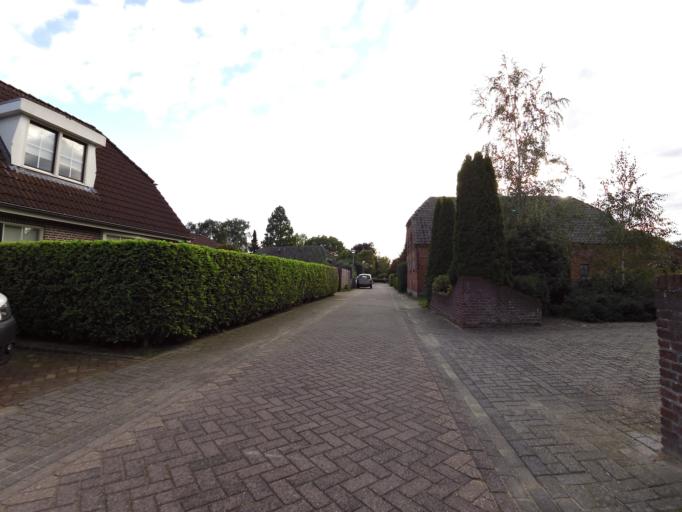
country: NL
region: Gelderland
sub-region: Gemeente Montferland
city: s-Heerenberg
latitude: 51.8793
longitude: 6.2689
